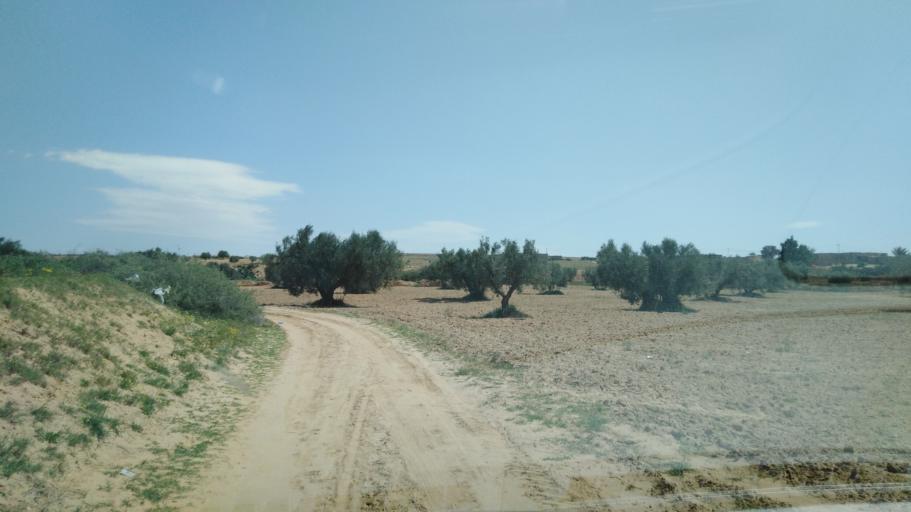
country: TN
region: Safaqis
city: Sfax
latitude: 34.7798
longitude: 10.5271
